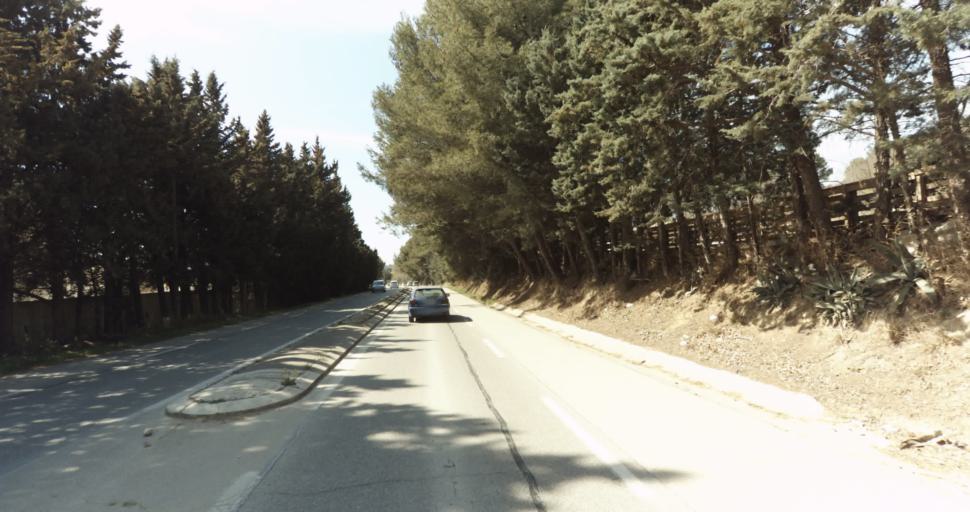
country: FR
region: Provence-Alpes-Cote d'Azur
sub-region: Departement des Bouches-du-Rhone
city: Ventabren
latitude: 43.5462
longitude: 5.2845
